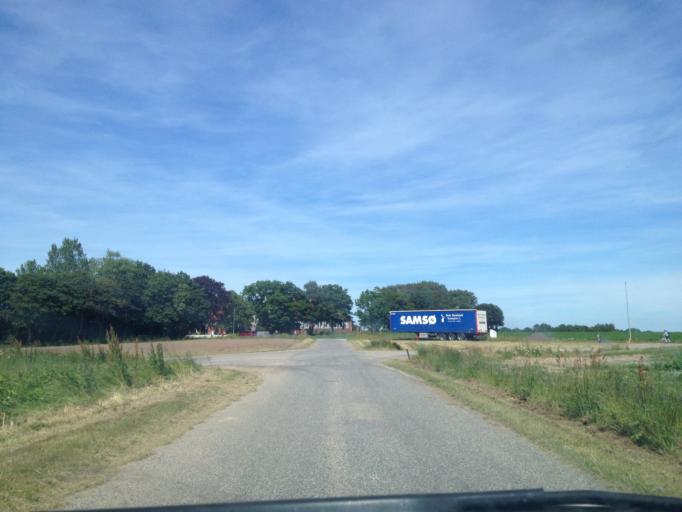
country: DK
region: Central Jutland
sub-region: Samso Kommune
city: Tranebjerg
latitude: 55.9573
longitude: 10.5537
